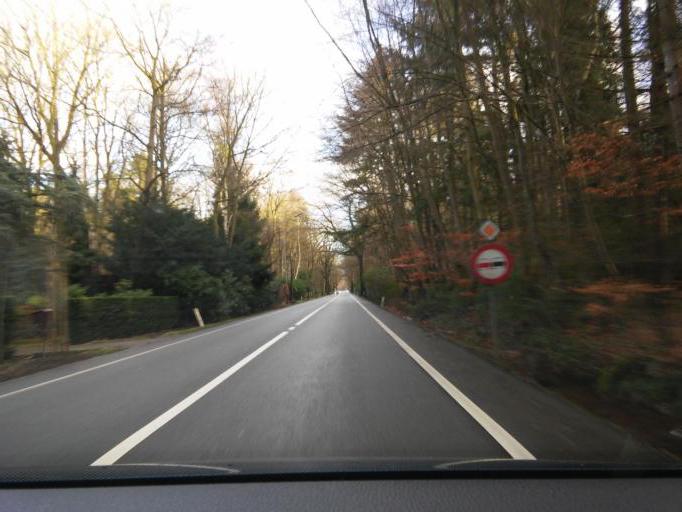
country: BE
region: Flanders
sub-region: Provincie Antwerpen
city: Kapellen
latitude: 51.3584
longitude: 4.4261
